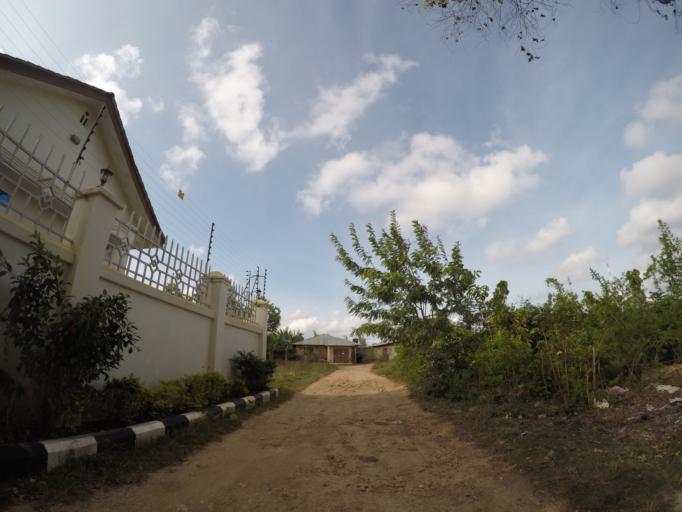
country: TZ
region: Zanzibar Central/South
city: Koani
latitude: -6.2272
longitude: 39.3156
